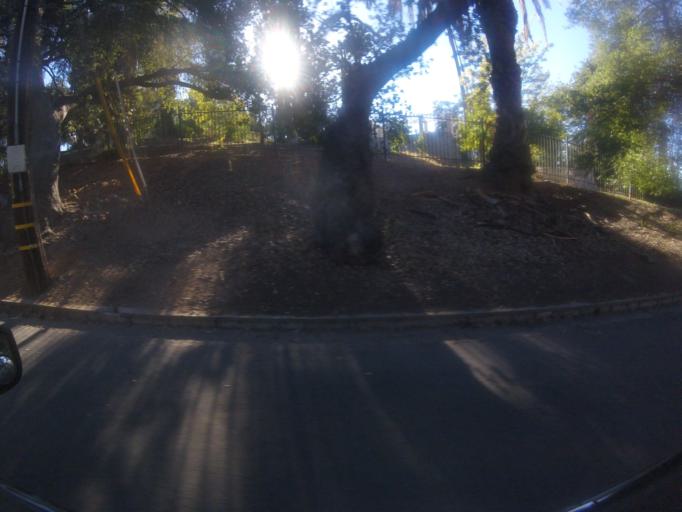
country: US
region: California
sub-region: San Bernardino County
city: Redlands
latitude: 34.0316
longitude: -117.1815
